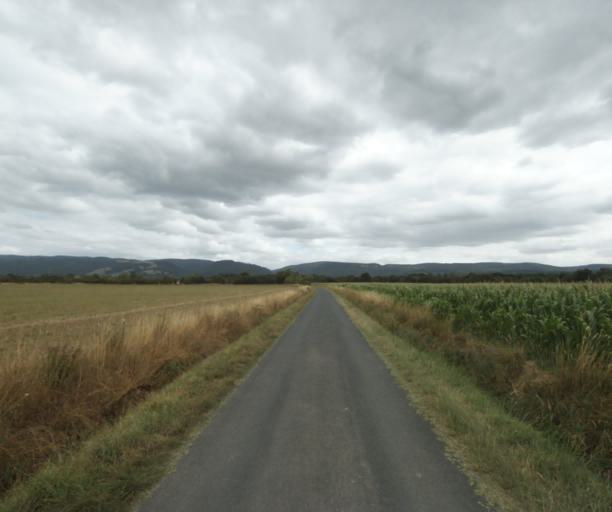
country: FR
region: Midi-Pyrenees
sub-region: Departement de la Haute-Garonne
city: Revel
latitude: 43.4761
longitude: 2.0340
